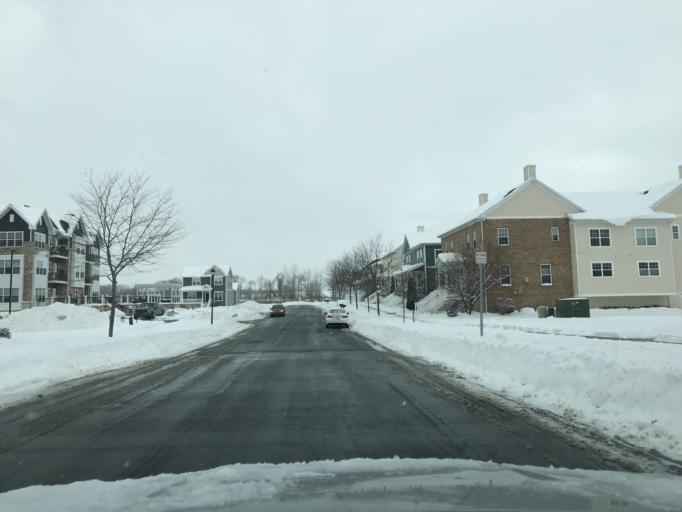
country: US
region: Wisconsin
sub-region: Dane County
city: Sun Prairie
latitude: 43.1673
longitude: -89.2774
